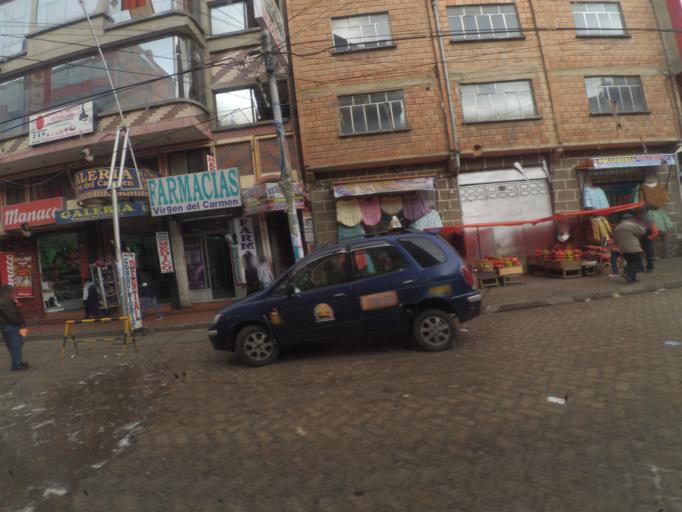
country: BO
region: La Paz
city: La Paz
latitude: -16.5070
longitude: -68.1623
